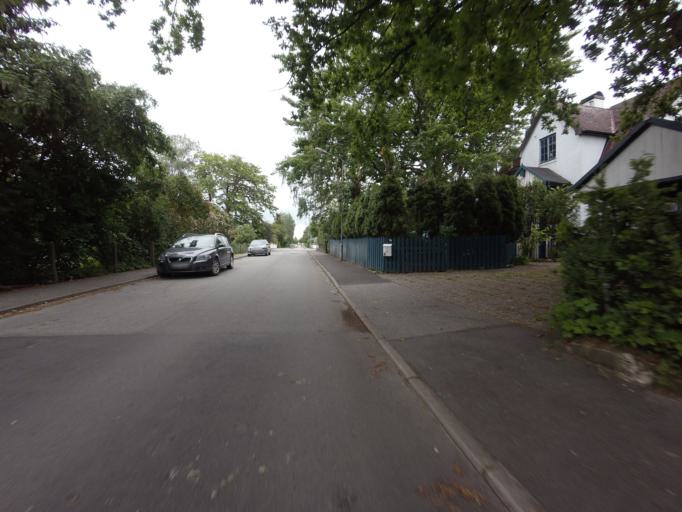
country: SE
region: Skane
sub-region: Staffanstorps Kommun
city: Hjaerup
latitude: 55.6526
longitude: 13.1181
